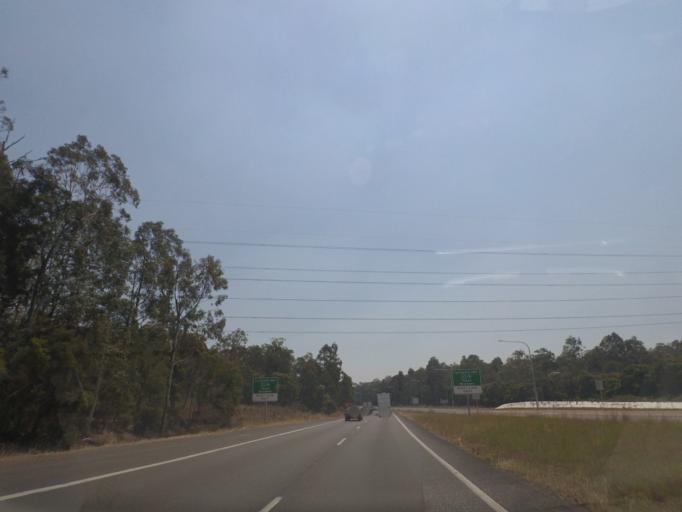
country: AU
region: New South Wales
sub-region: Newcastle
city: Beresfield
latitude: -32.8190
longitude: 151.6346
